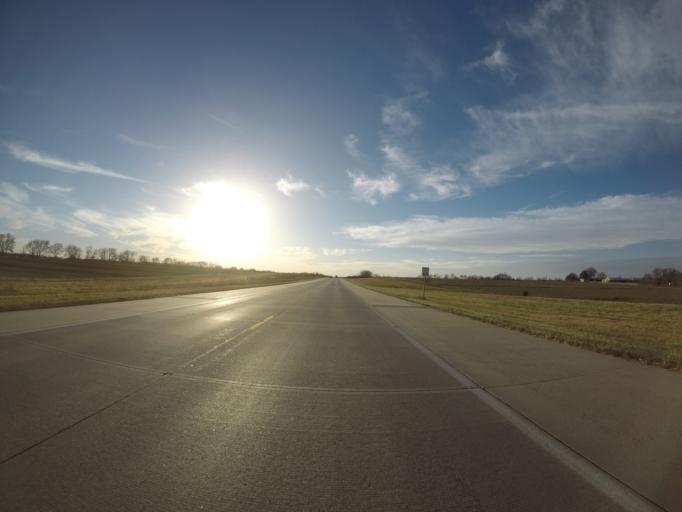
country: US
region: Kansas
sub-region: Lyon County
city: Emporia
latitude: 38.4113
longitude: -96.2836
